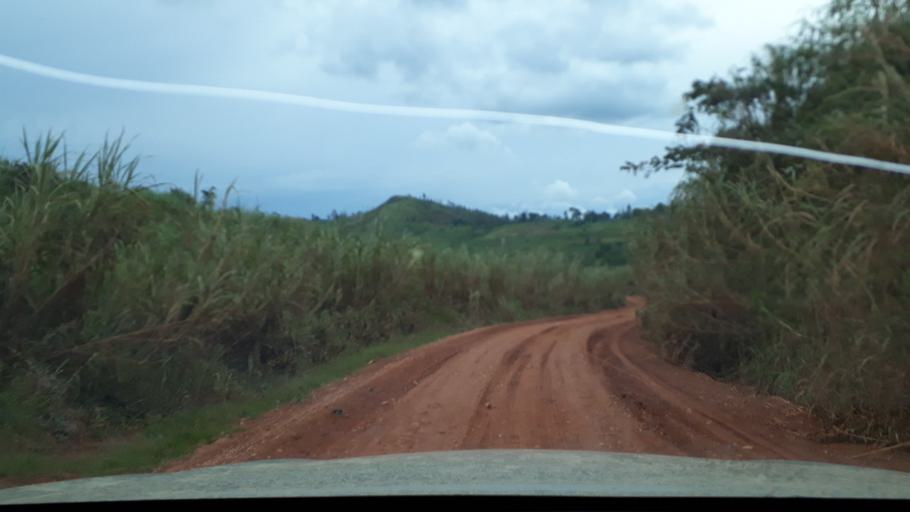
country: CD
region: Eastern Province
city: Bunia
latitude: 1.7693
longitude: 30.3864
